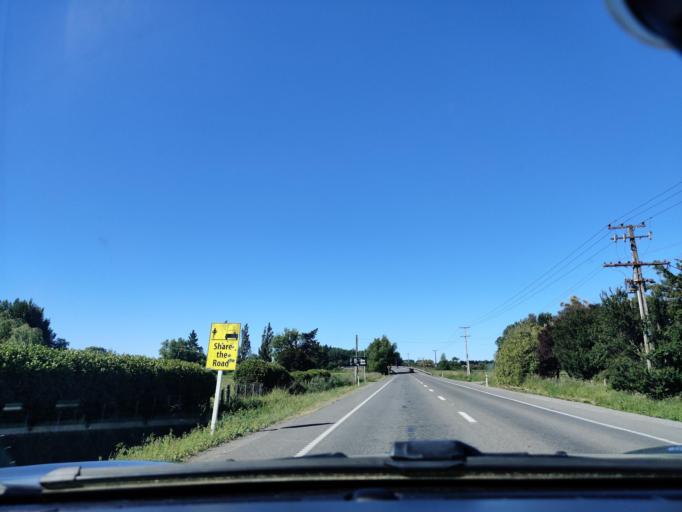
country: NZ
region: Wellington
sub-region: Masterton District
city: Masterton
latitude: -41.0619
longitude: 175.4914
